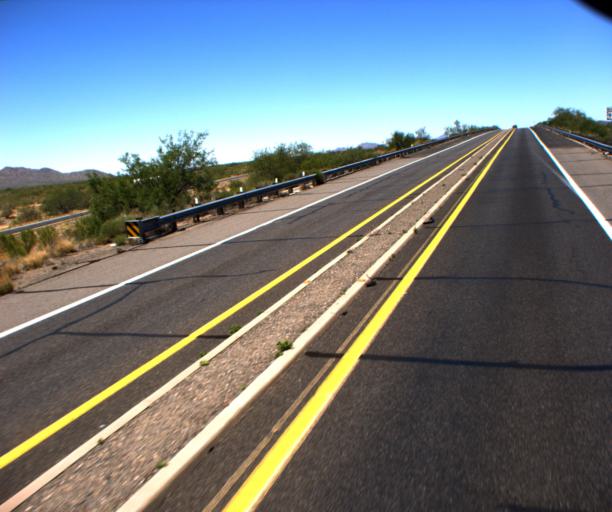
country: US
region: Arizona
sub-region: Yavapai County
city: Congress
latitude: 34.1217
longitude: -112.9481
